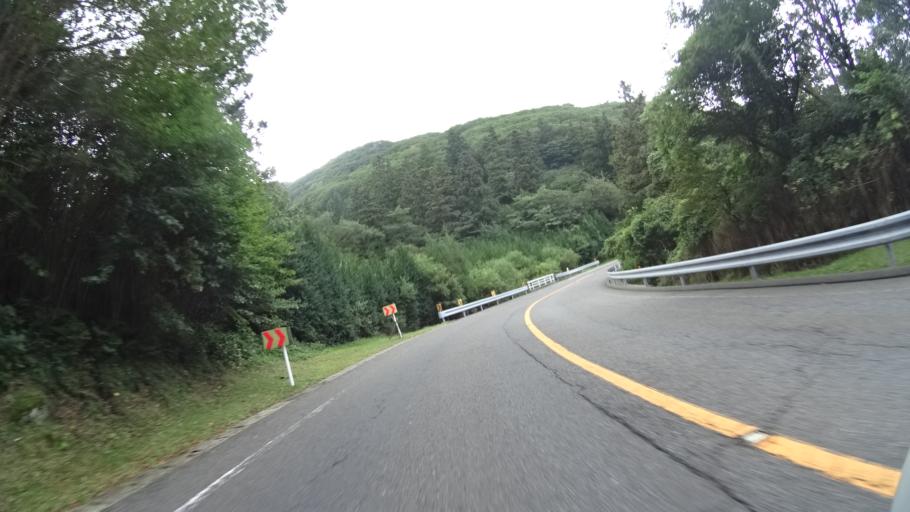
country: JP
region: Oita
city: Tsukawaki
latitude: 33.0982
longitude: 131.2215
